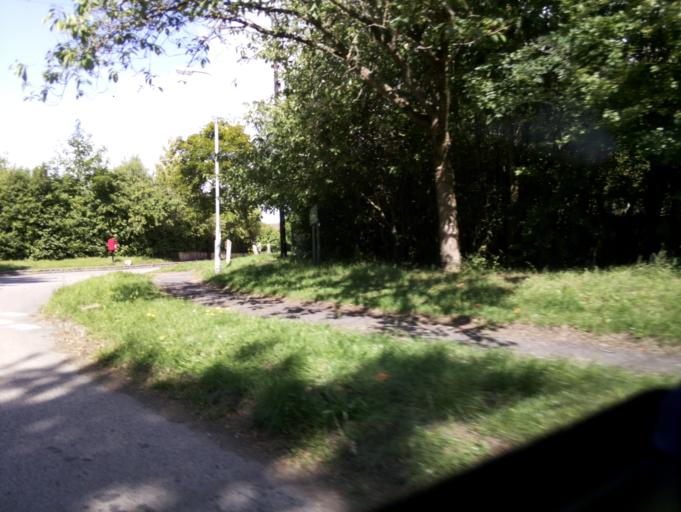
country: GB
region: England
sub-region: Northamptonshire
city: Deanshanger
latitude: 51.9970
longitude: -0.9226
